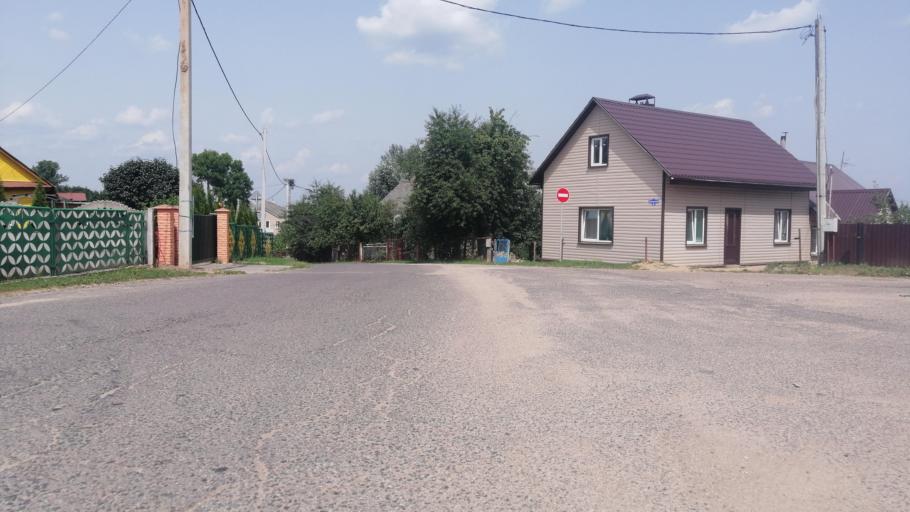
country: BY
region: Grodnenskaya
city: Navahrudak
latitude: 53.6008
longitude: 25.8346
